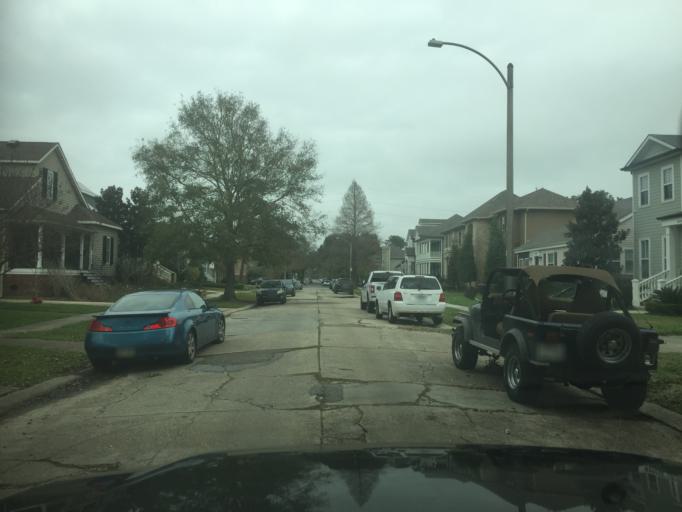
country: US
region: Louisiana
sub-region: Jefferson Parish
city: Metairie
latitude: 29.9992
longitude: -90.1044
